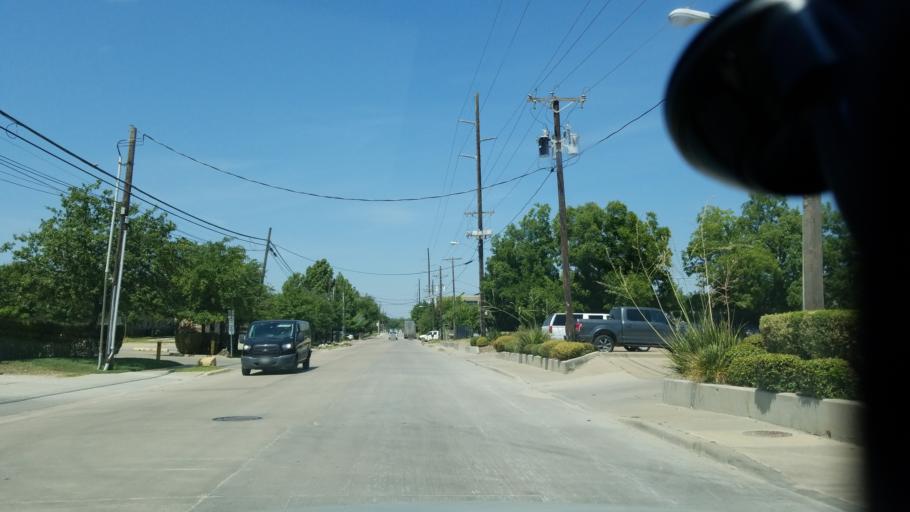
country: US
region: Texas
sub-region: Dallas County
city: Farmers Branch
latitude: 32.8930
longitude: -96.9034
